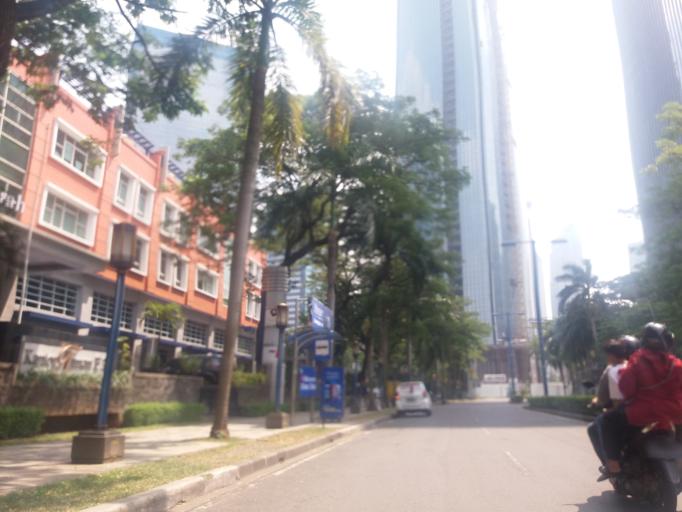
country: ID
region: Jakarta Raya
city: Jakarta
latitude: -6.2311
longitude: 106.8280
